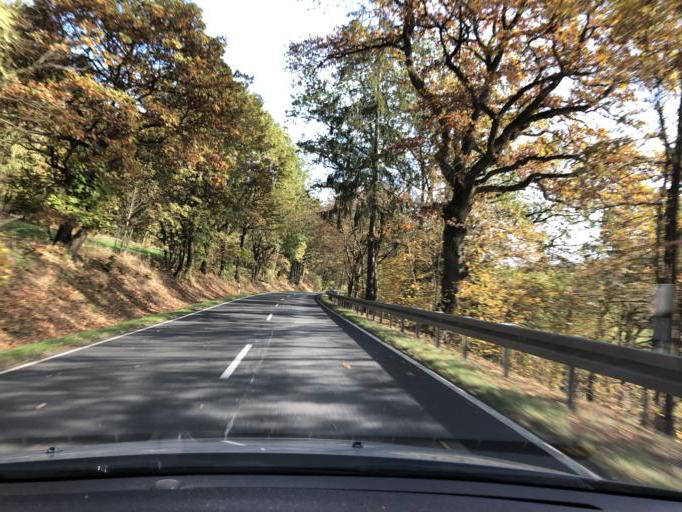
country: DE
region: Thuringia
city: Kloster Vessra
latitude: 50.4919
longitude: 10.6669
